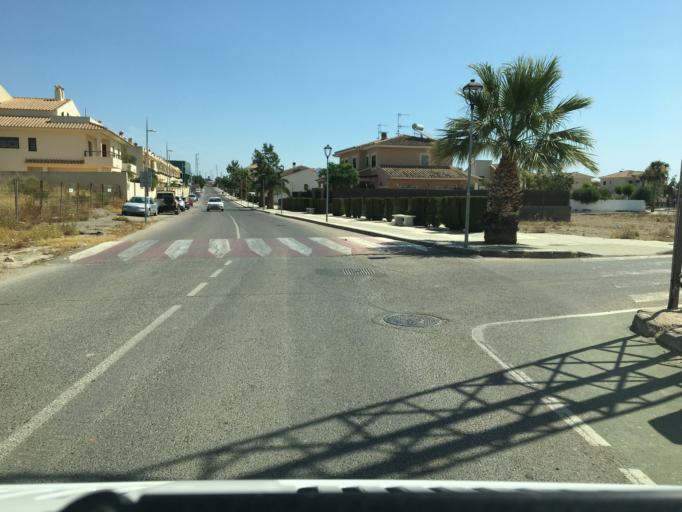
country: ES
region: Andalusia
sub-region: Provincia de Almeria
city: Huercal-Overa
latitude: 37.4069
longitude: -1.9312
